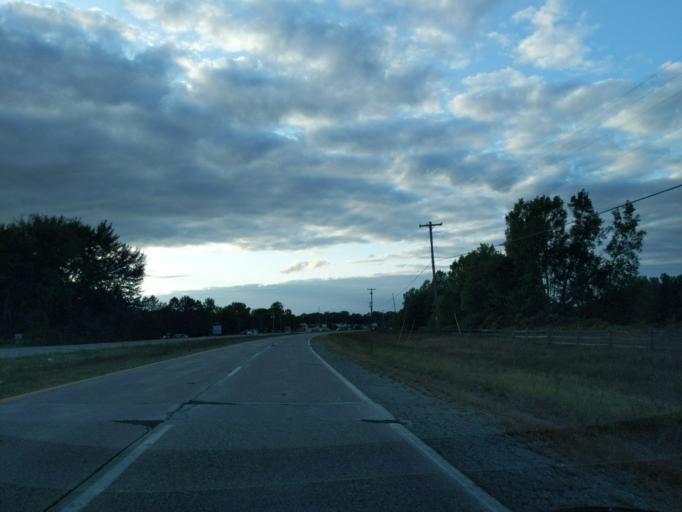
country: US
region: Michigan
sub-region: Ingham County
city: Holt
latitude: 42.6150
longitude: -84.4954
